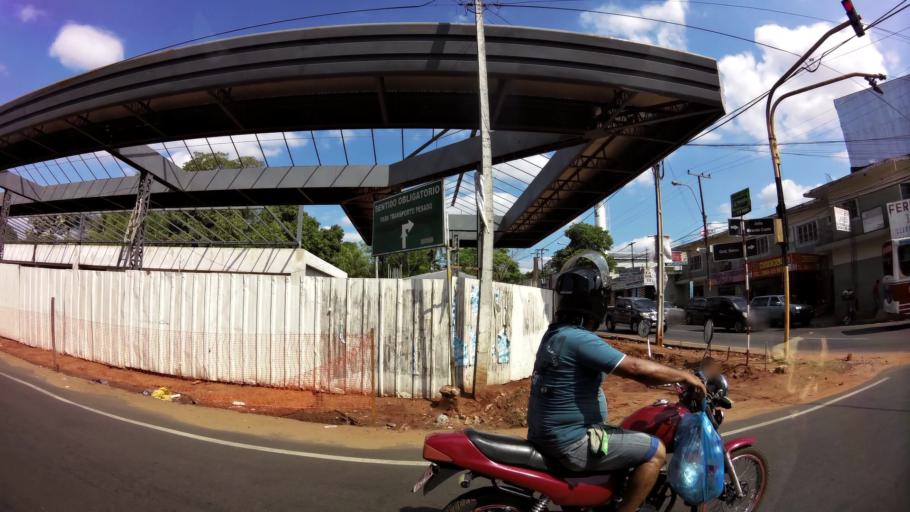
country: PY
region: Central
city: San Lorenzo
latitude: -25.3418
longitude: -57.5037
